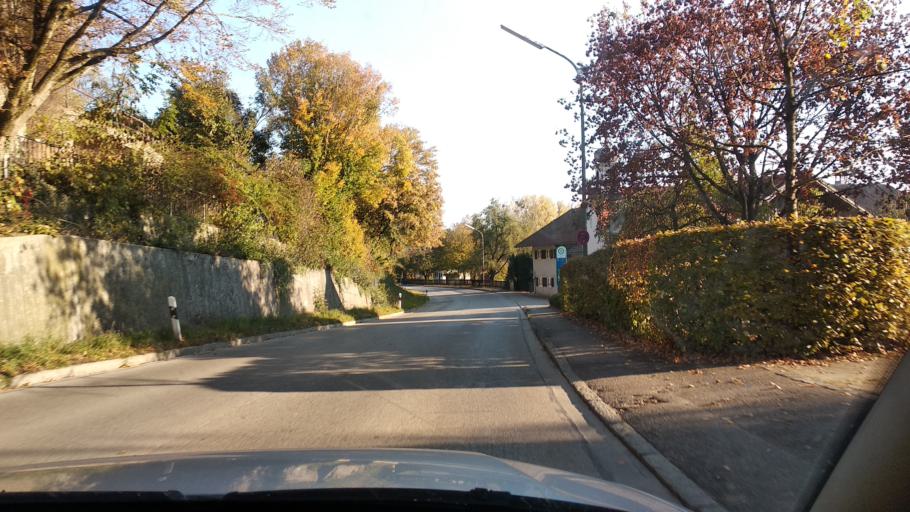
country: DE
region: Bavaria
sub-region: Upper Bavaria
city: Oberpframmern
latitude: 47.9955
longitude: 11.8293
